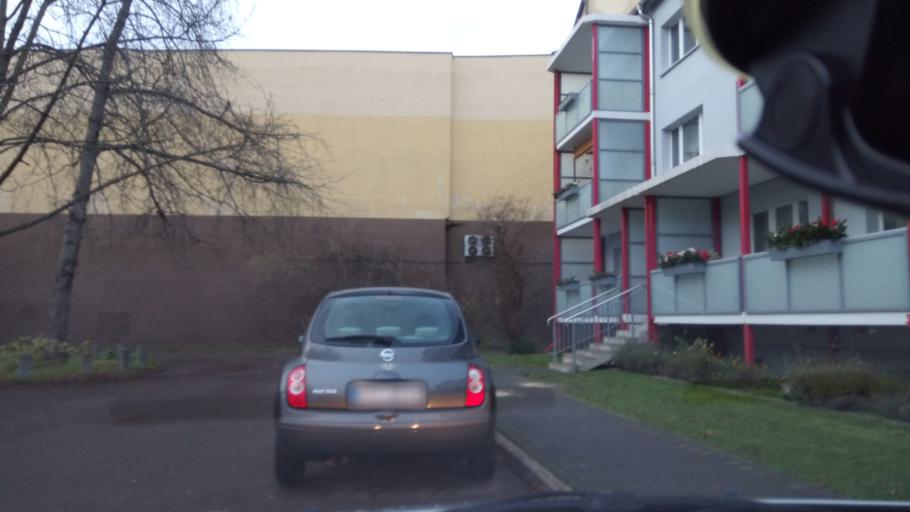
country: DE
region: Saxony
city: Bitterfeld-Wolfen
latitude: 51.6225
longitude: 12.3320
